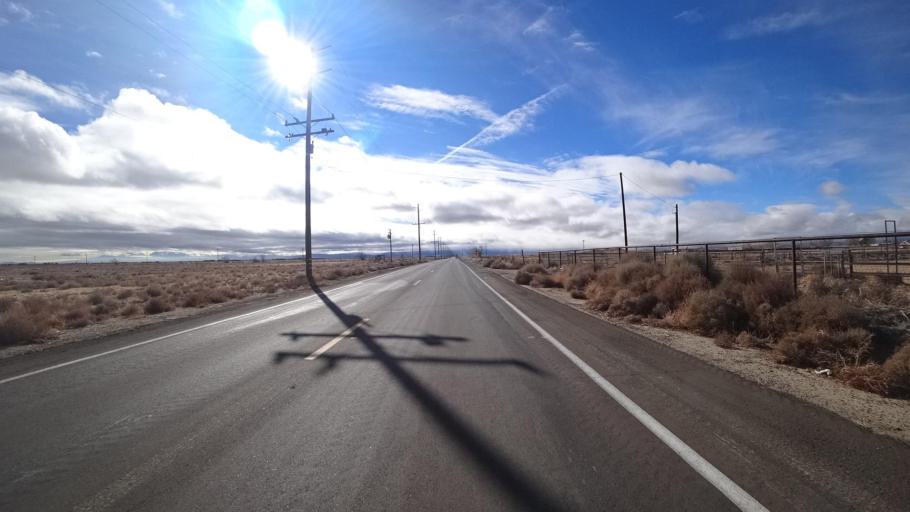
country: US
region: California
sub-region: Kern County
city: Rosamond
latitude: 34.8226
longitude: -118.2905
